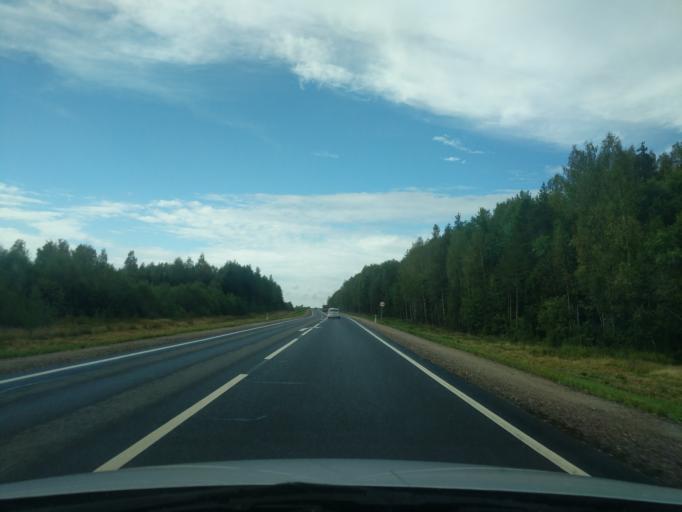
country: RU
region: Kostroma
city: Ostrovskoye
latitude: 57.8149
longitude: 41.9743
